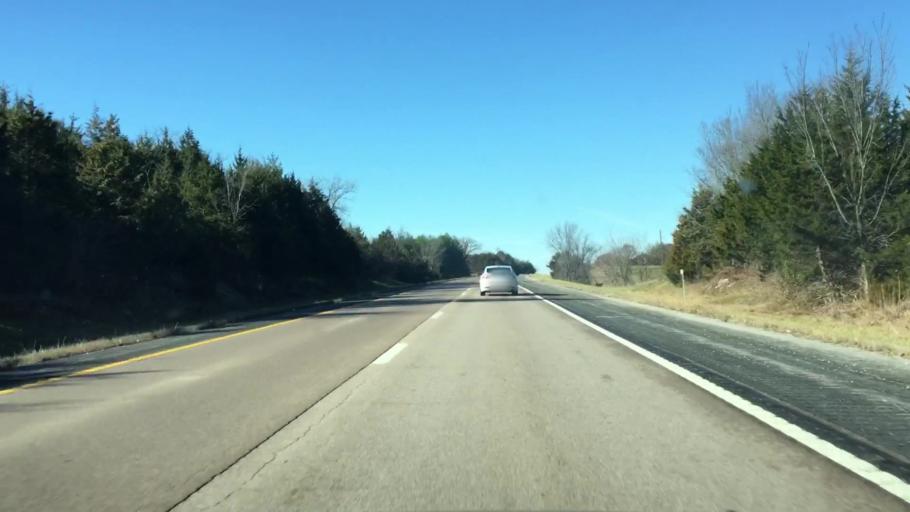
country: US
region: Missouri
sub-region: Miller County
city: Eldon
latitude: 38.3687
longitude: -92.4707
